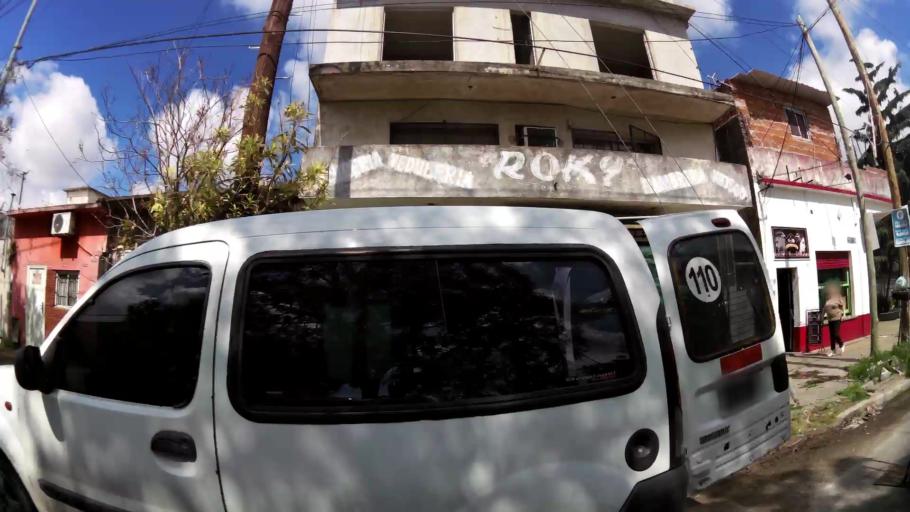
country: AR
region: Buenos Aires
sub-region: Partido de Lanus
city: Lanus
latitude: -34.6778
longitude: -58.4236
